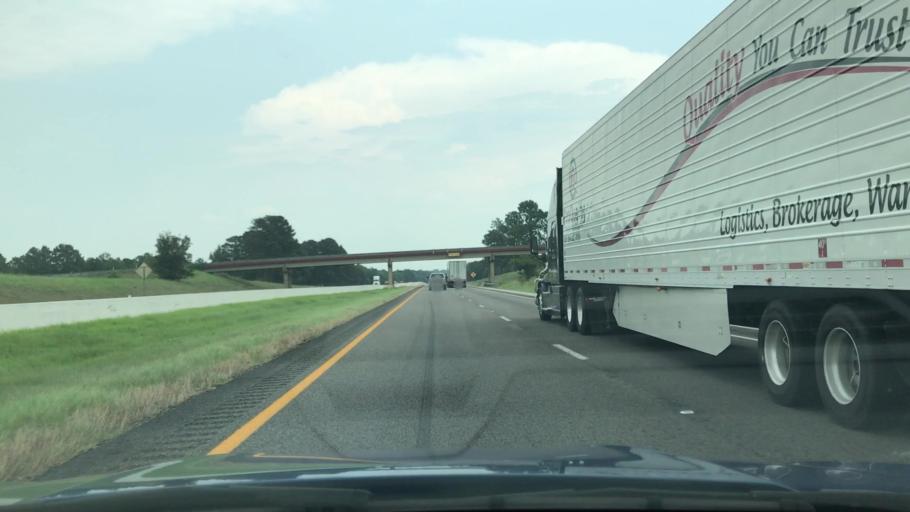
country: US
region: Texas
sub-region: Gregg County
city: Liberty City
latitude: 32.4364
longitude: -94.9915
